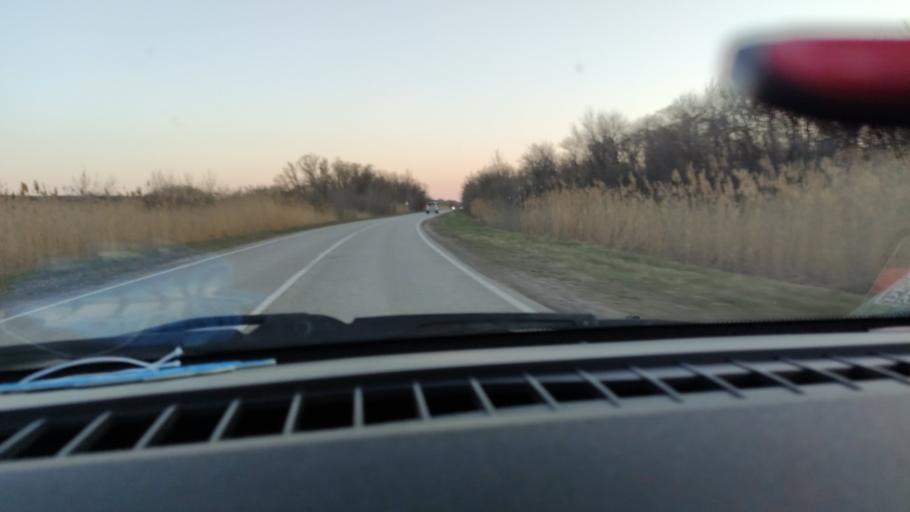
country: RU
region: Saratov
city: Privolzhskiy
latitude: 51.2548
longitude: 45.9415
